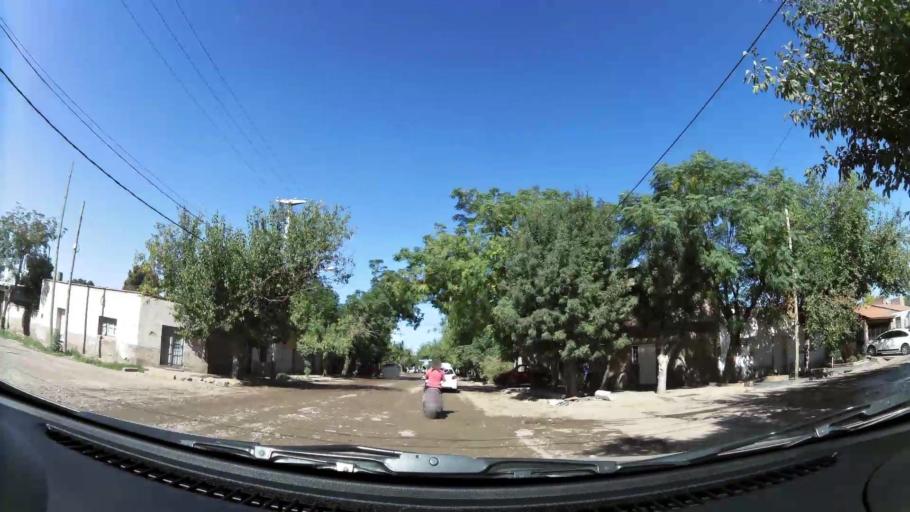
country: AR
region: Mendoza
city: Villa Nueva
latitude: -32.8943
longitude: -68.8035
